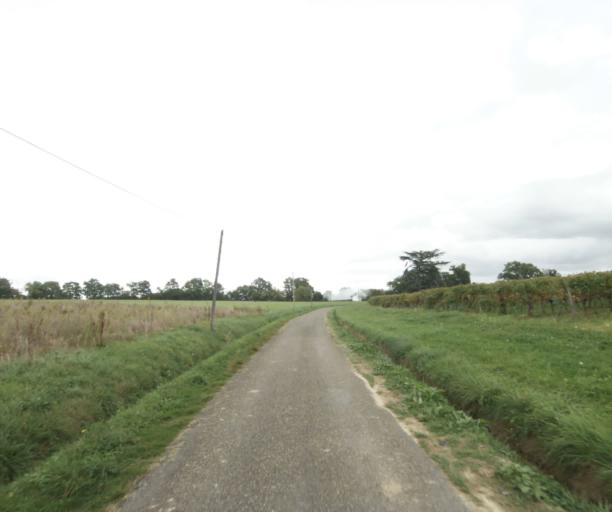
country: FR
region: Midi-Pyrenees
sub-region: Departement du Gers
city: Eauze
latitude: 43.8886
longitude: 0.1292
